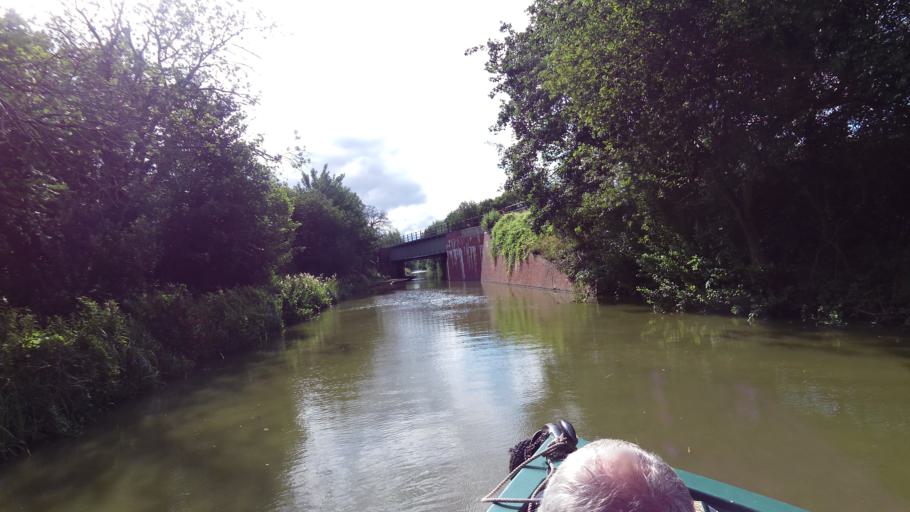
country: GB
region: England
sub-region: West Berkshire
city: Kintbury
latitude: 51.4092
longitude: -1.4745
